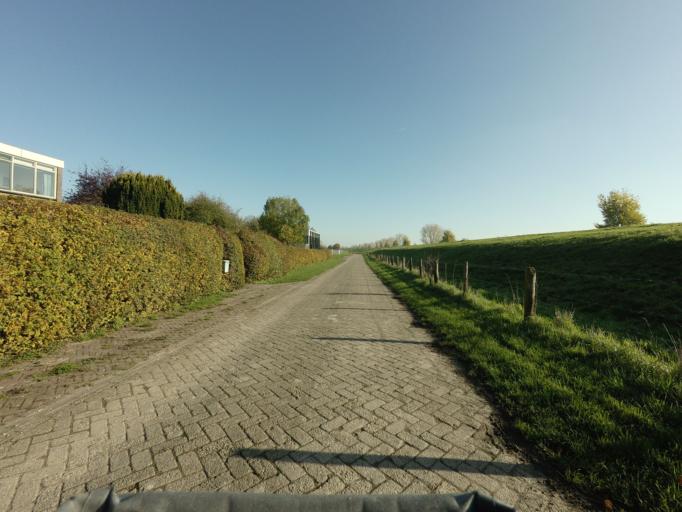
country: NL
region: North Brabant
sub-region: Gemeente Waalwijk
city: Waalwijk
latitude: 51.7142
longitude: 5.0108
